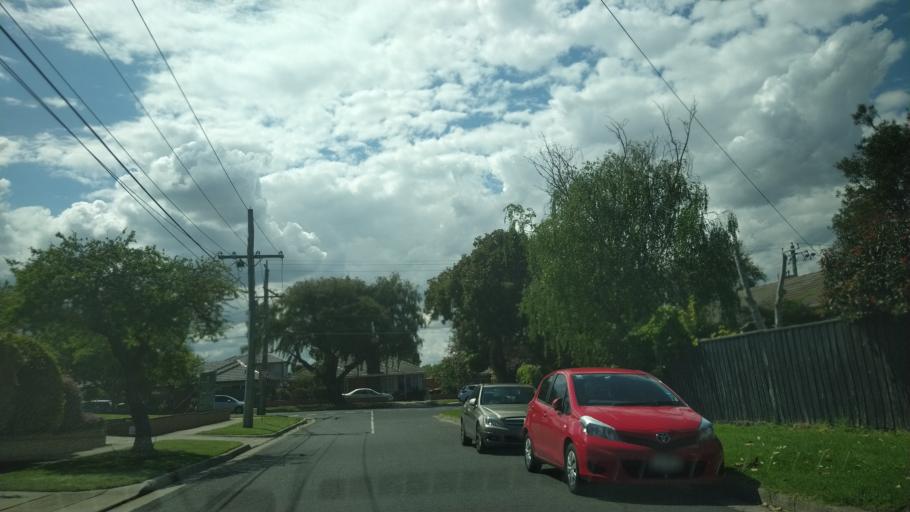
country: AU
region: Victoria
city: Highett
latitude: -37.9464
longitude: 145.0485
